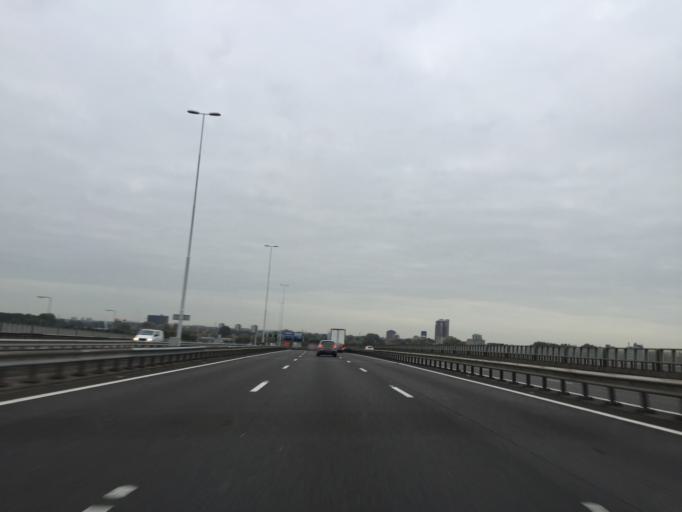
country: NL
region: South Holland
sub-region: Gemeente Rotterdam
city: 's-Gravenland
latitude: 51.9021
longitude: 4.5439
